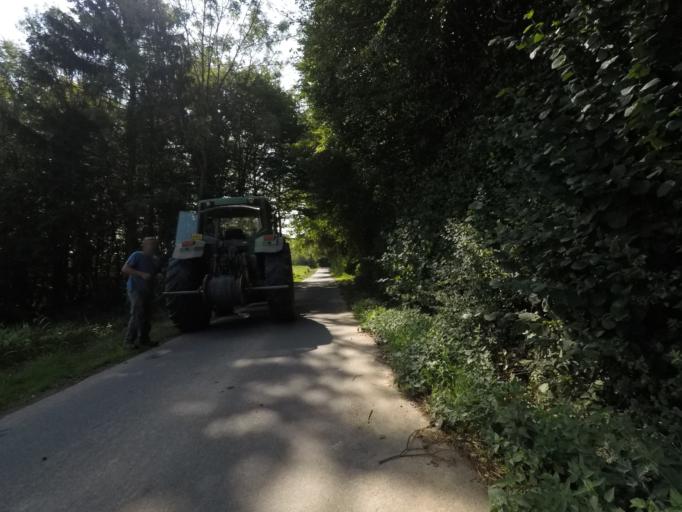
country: LU
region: Luxembourg
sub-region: Canton de Luxembourg
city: Olm
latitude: 49.6529
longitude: 6.0209
